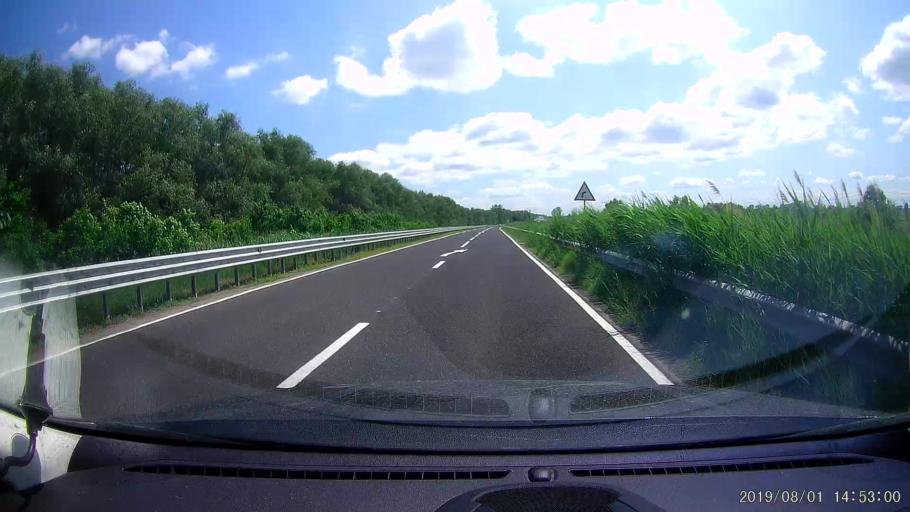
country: RO
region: Braila
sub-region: Comuna Vadeni
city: Vadeni
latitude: 45.3450
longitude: 28.0076
